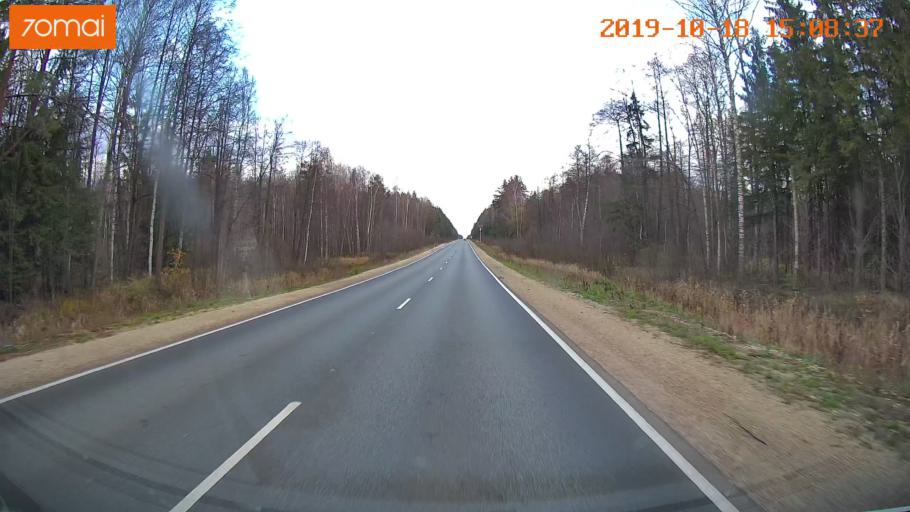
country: RU
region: Vladimir
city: Gus'-Khrustal'nyy
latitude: 55.5548
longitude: 40.6124
